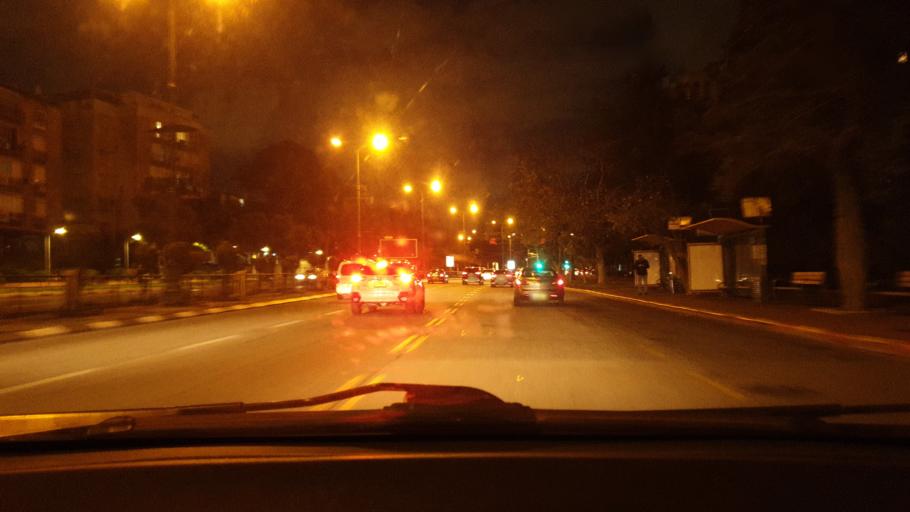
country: IL
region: Central District
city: Rishon LeZiyyon
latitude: 31.9572
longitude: 34.8023
